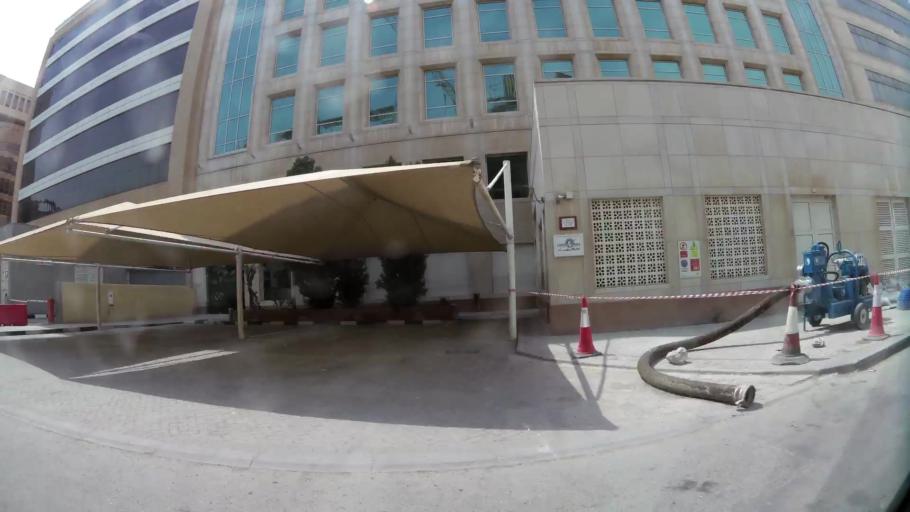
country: QA
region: Baladiyat ad Dawhah
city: Doha
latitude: 25.2821
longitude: 51.5358
